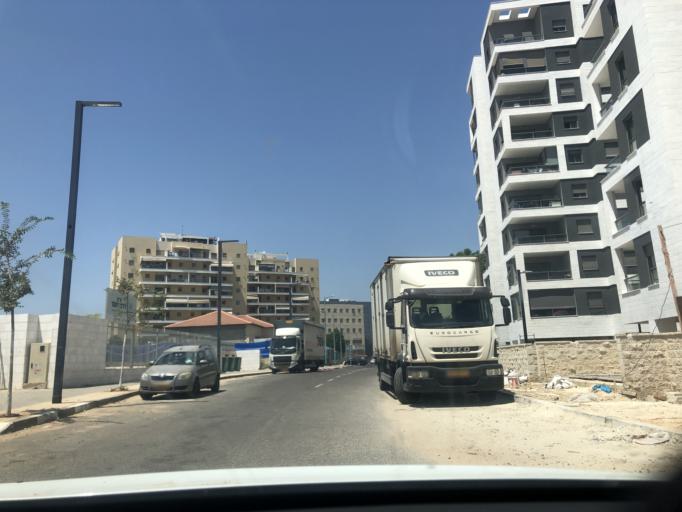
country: IL
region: Central District
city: Lod
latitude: 31.9430
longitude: 34.9010
